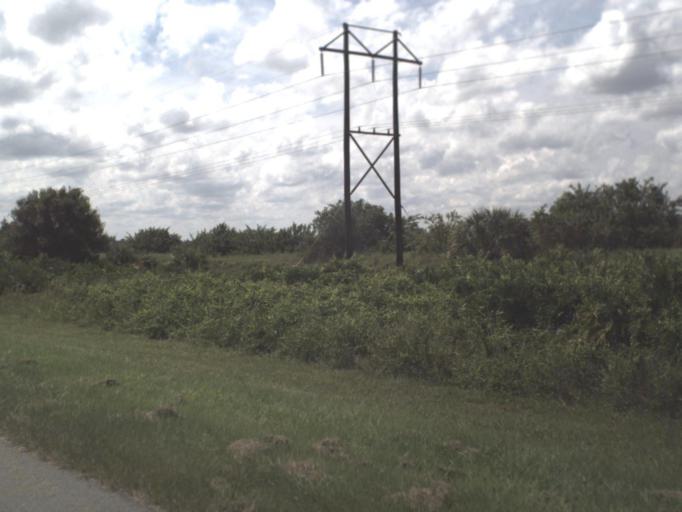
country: US
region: Florida
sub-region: Collier County
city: Immokalee
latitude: 26.3278
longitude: -81.3432
